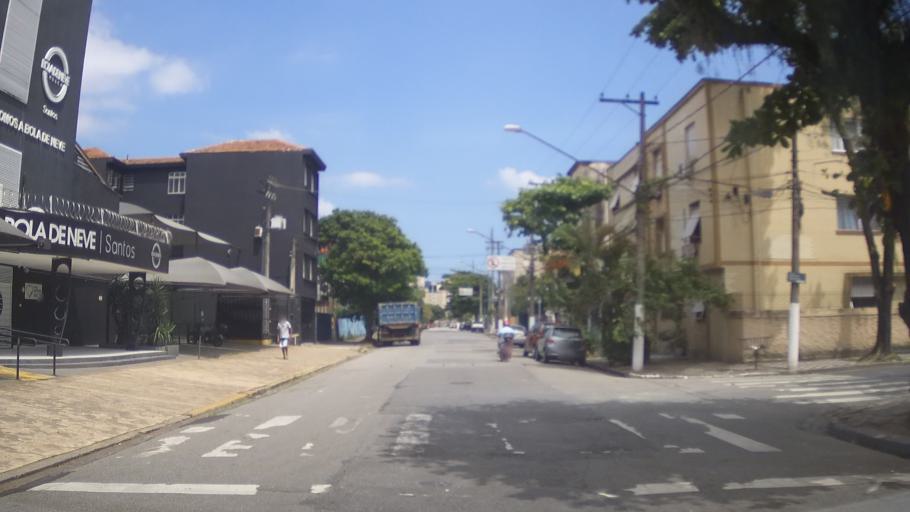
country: BR
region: Sao Paulo
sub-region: Santos
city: Santos
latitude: -23.9568
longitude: -46.3143
